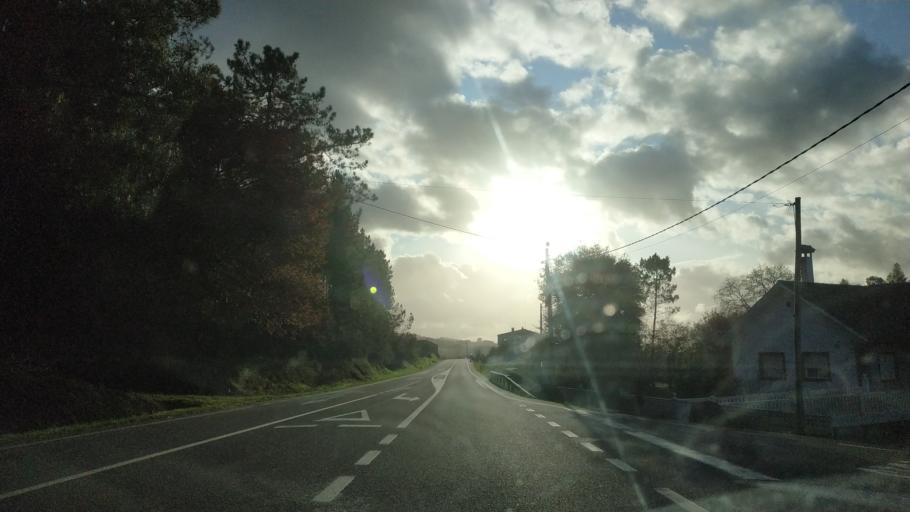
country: ES
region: Galicia
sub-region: Provincia de Pontevedra
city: Silleda
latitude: 42.7863
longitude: -8.1681
